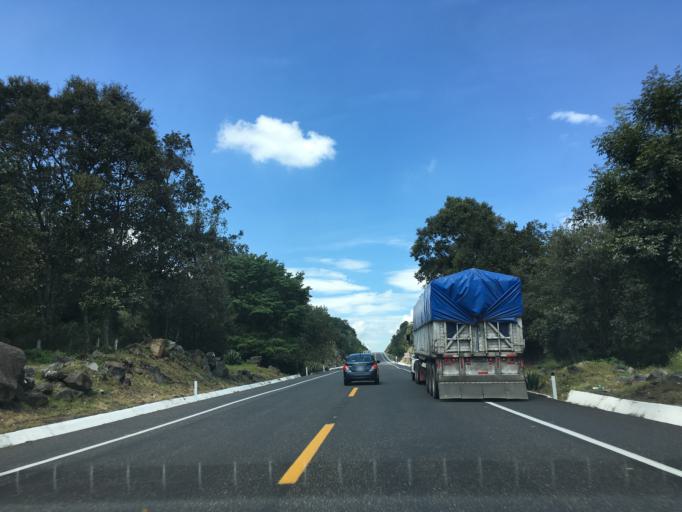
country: MX
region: Michoacan
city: Patzcuaro
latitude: 19.4962
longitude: -101.6253
